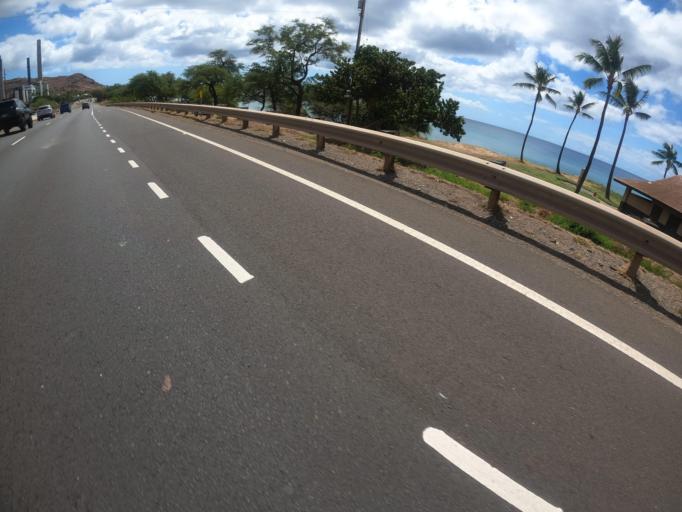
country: US
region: Hawaii
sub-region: Honolulu County
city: Nanakuli
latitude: 21.3610
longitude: -158.1319
